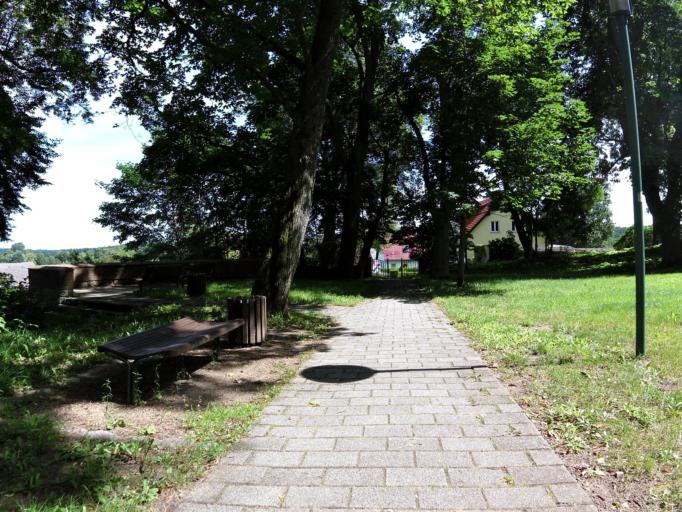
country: DE
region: Mecklenburg-Vorpommern
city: Loitz
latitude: 53.3359
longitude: 13.4374
